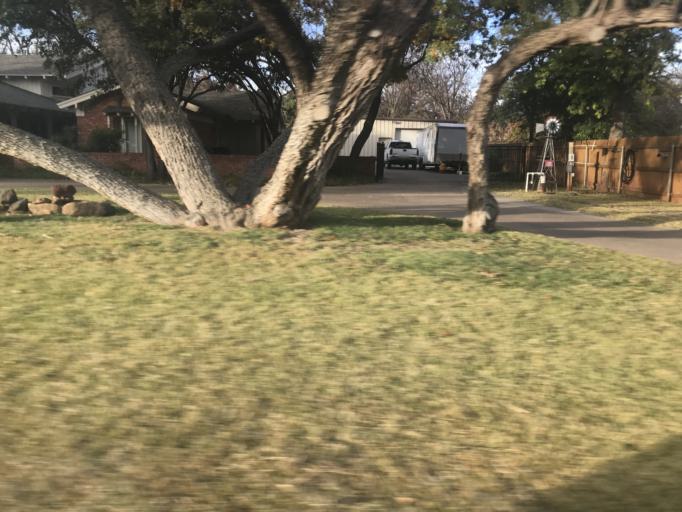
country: US
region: Texas
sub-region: Taylor County
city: Abilene
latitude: 32.4324
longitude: -99.7725
